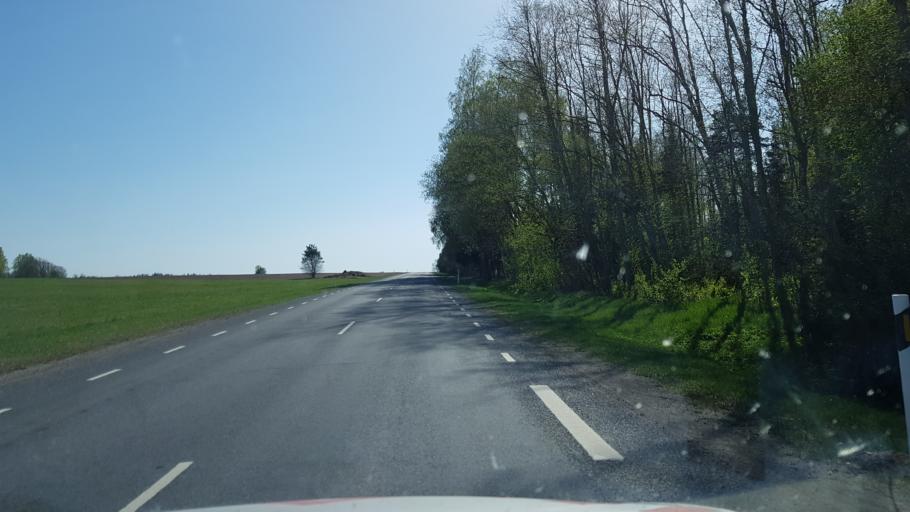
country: EE
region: Viljandimaa
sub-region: Viljandi linn
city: Viljandi
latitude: 58.3208
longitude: 25.5707
